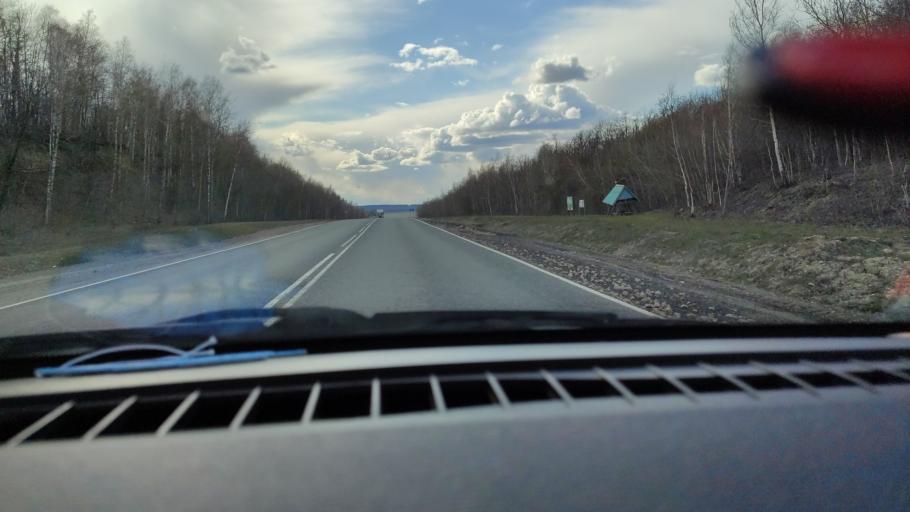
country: RU
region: Saratov
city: Vol'sk
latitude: 52.1125
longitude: 47.3208
